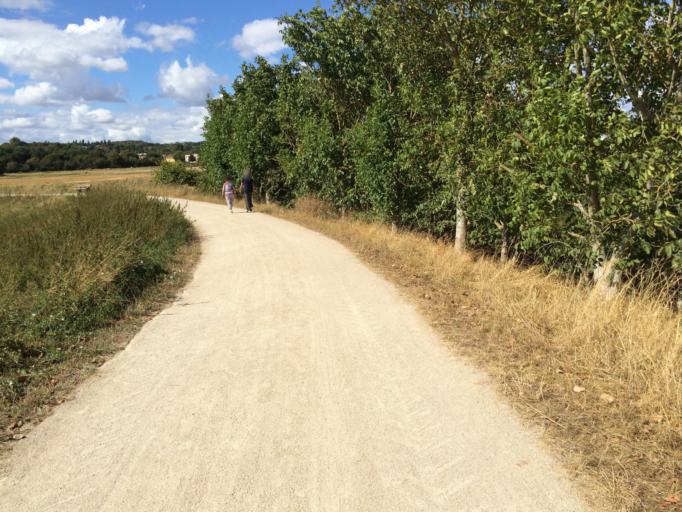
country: FR
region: Ile-de-France
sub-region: Departement de l'Essonne
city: Champlan
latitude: 48.6989
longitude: 2.2837
